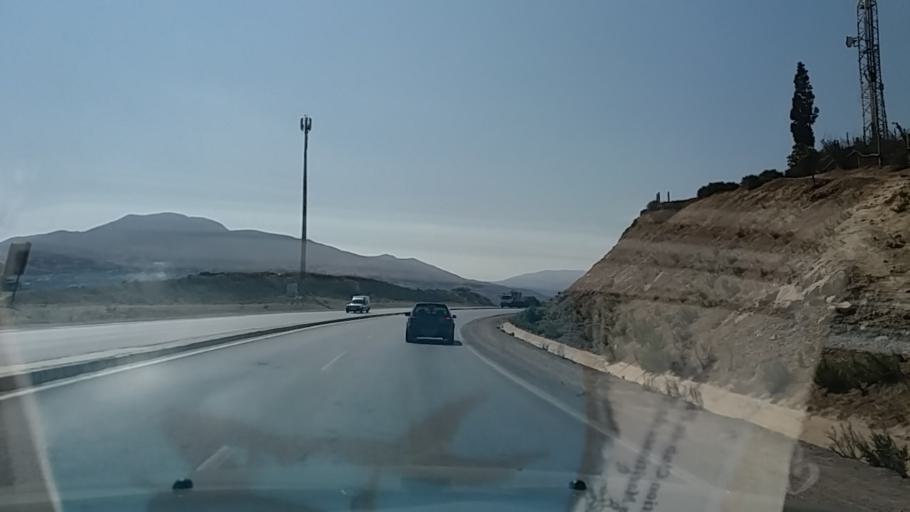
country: MA
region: Tanger-Tetouan
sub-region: Tetouan
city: Saddina
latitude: 35.5583
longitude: -5.4477
